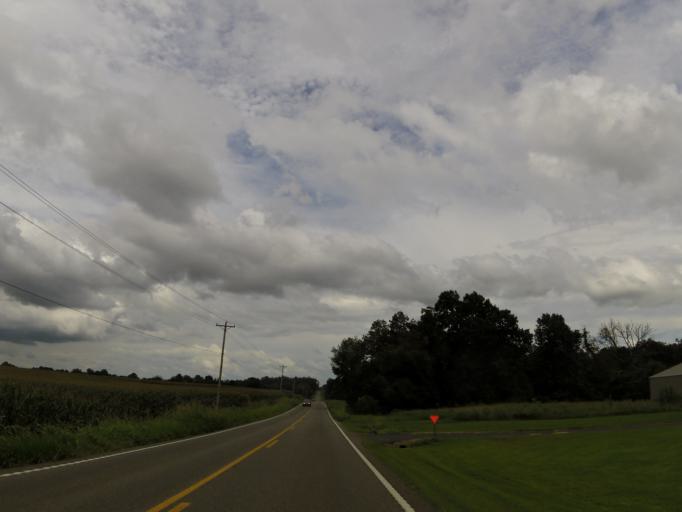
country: US
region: Kentucky
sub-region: Ballard County
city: La Center
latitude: 36.9909
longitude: -88.9074
